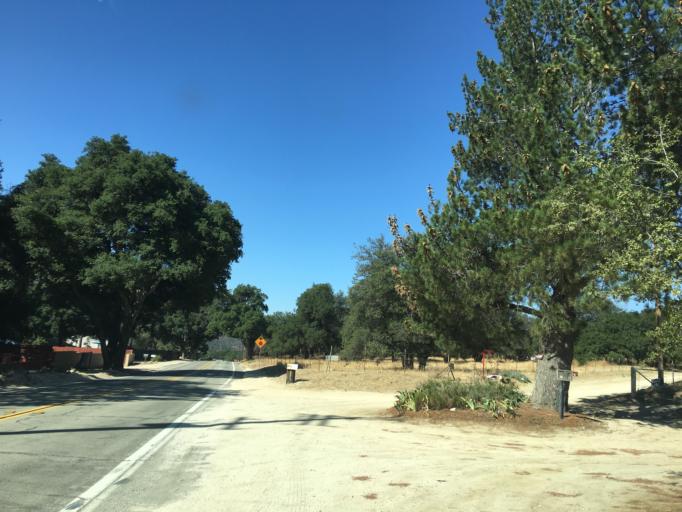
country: US
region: California
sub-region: Los Angeles County
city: Green Valley
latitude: 34.6238
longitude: -118.4121
